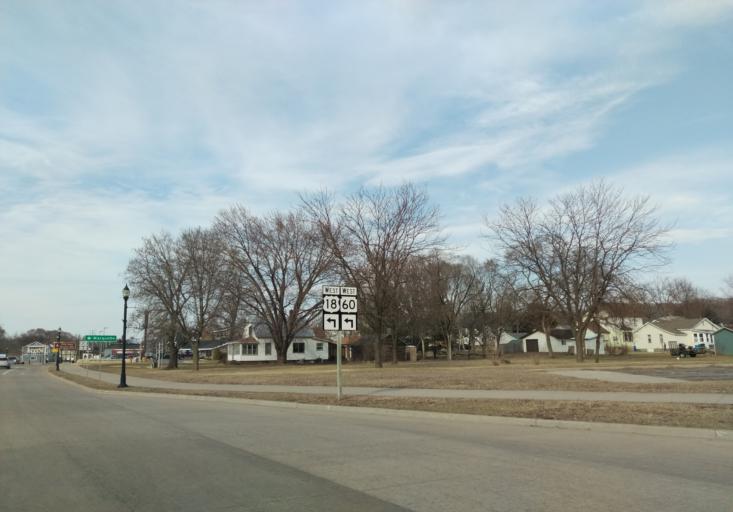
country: US
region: Wisconsin
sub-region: Crawford County
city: Prairie du Chien
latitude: 43.0491
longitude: -91.1492
